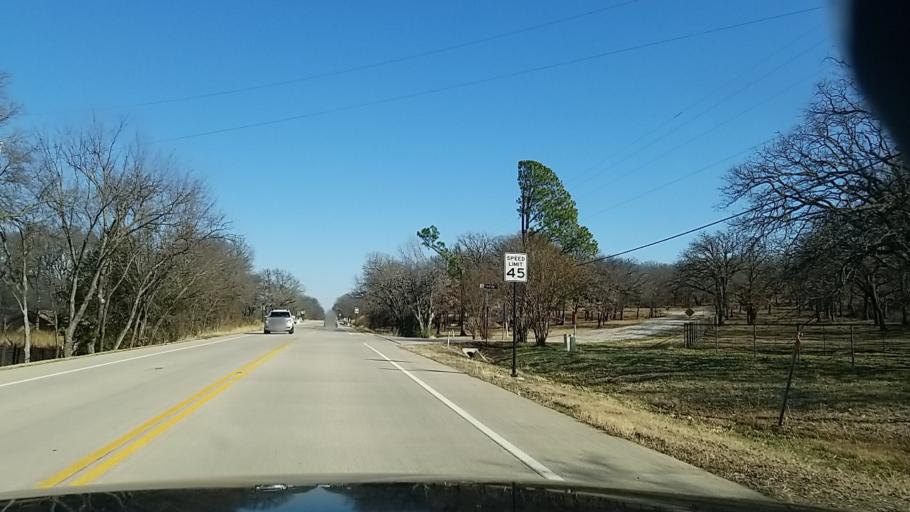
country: US
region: Texas
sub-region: Denton County
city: Argyle
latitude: 33.1336
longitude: -97.1698
